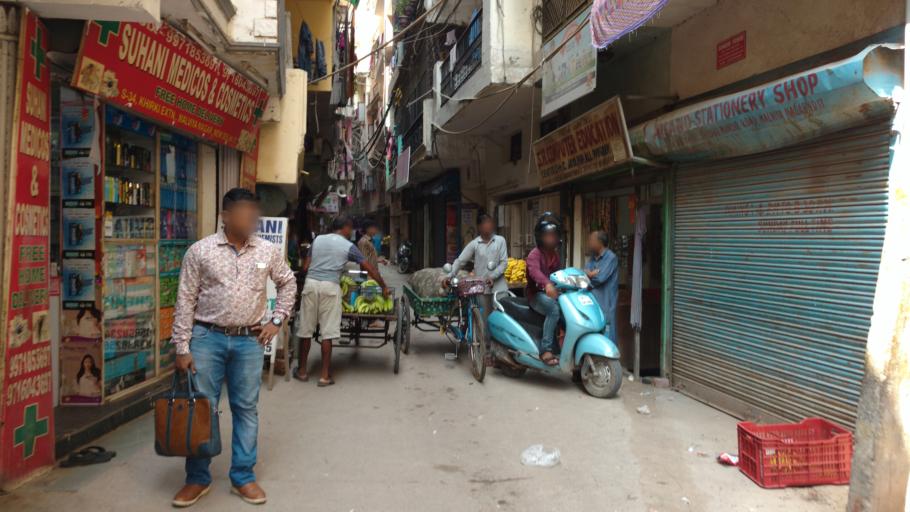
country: IN
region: NCT
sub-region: New Delhi
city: New Delhi
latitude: 28.5310
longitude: 77.2168
